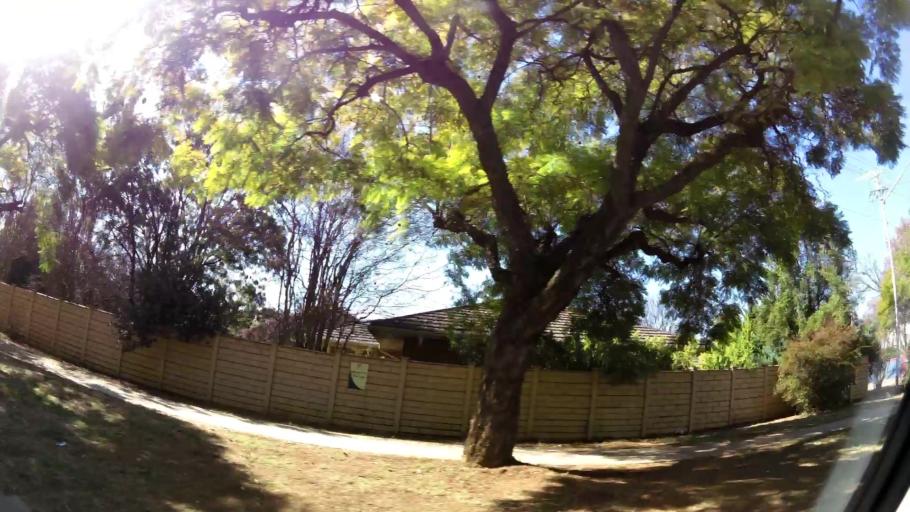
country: ZA
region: Gauteng
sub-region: City of Tshwane Metropolitan Municipality
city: Pretoria
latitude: -25.7665
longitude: 28.2490
